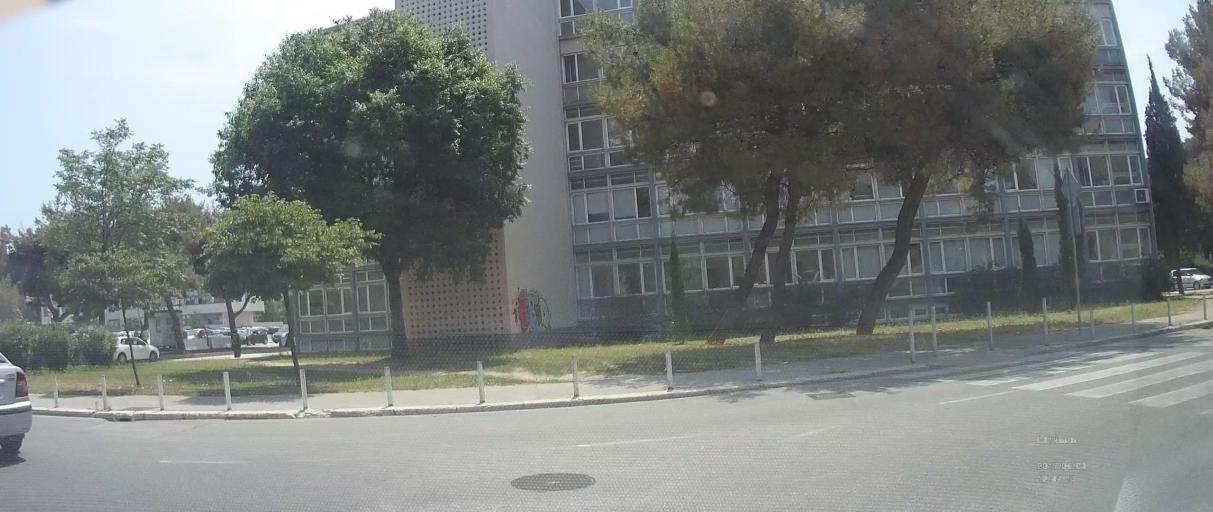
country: HR
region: Splitsko-Dalmatinska
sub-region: Grad Split
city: Split
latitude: 43.5166
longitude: 16.4395
